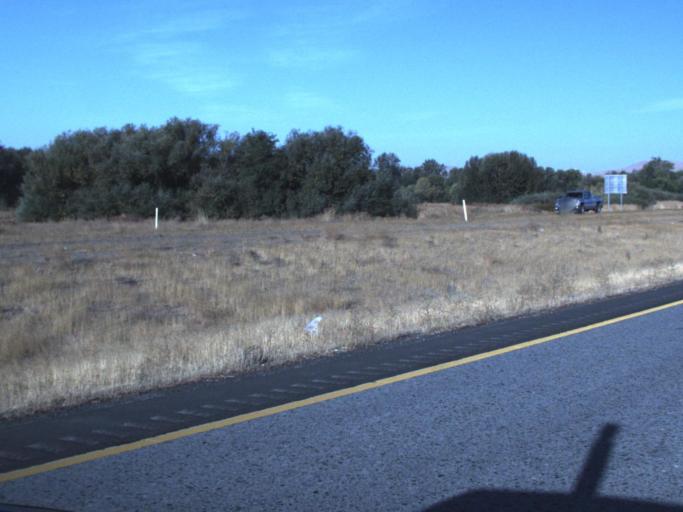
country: US
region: Washington
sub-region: Yakima County
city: Wapato
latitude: 46.4851
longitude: -120.4123
